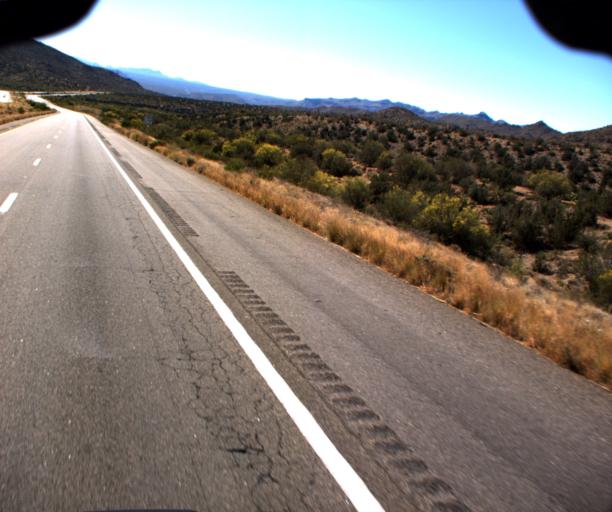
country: US
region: Arizona
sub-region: Yavapai County
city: Bagdad
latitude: 34.4311
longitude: -113.2522
